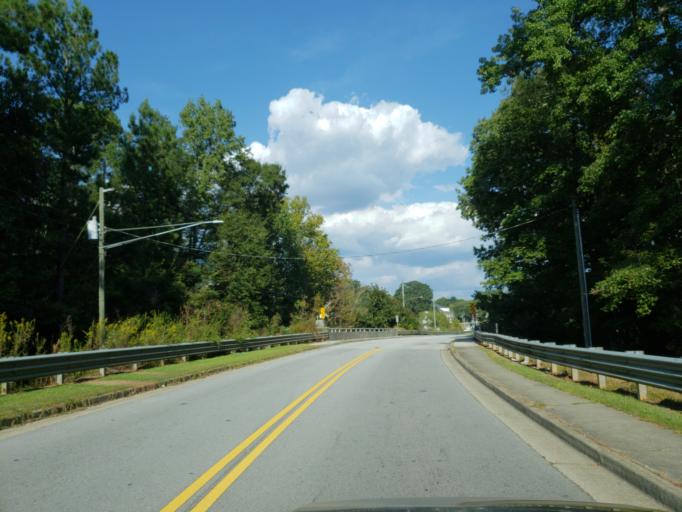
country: US
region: Georgia
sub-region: Cobb County
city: Powder Springs
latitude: 33.8590
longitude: -84.6889
